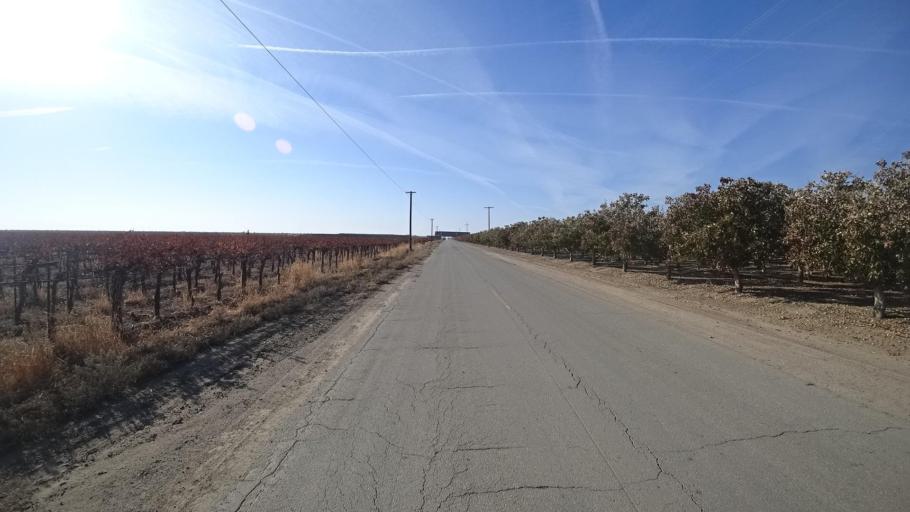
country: US
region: California
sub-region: Kern County
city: Wasco
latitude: 35.7032
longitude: -119.3441
